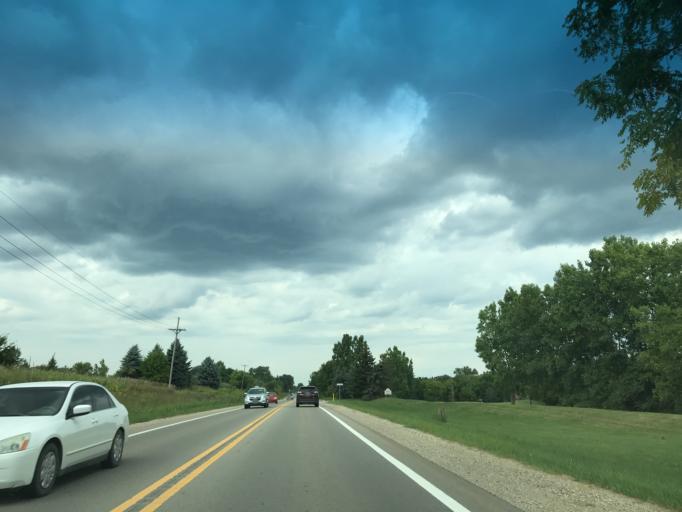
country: US
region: Michigan
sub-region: Oakland County
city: Milford
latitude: 42.5309
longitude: -83.6165
